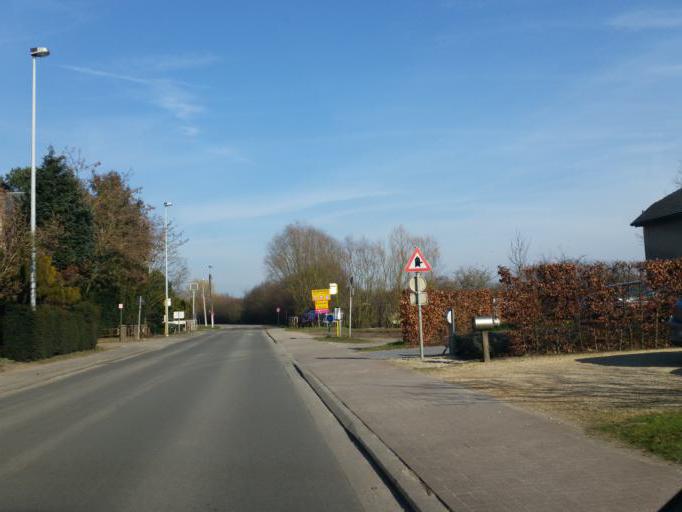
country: BE
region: Flanders
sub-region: Provincie Vlaams-Brabant
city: Boortmeerbeek
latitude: 50.9905
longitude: 4.5808
